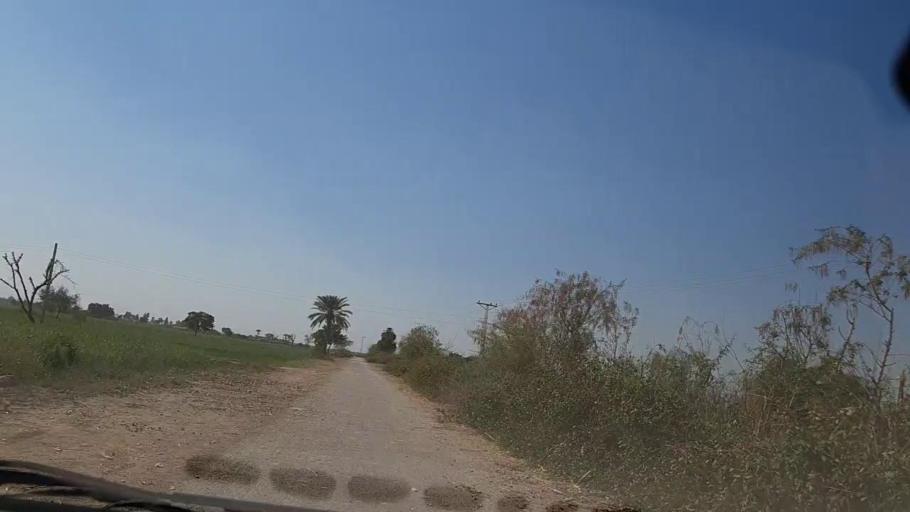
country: PK
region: Sindh
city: Mirwah Gorchani
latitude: 25.3726
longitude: 68.9977
